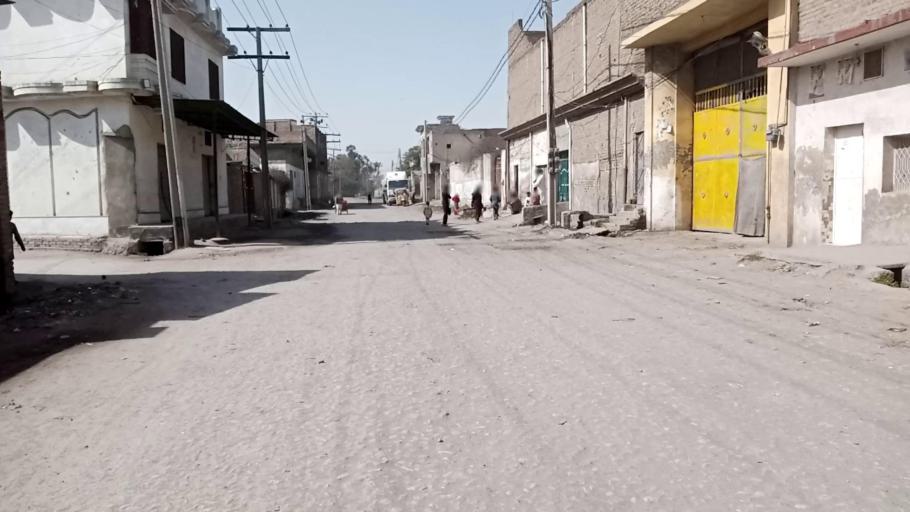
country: PK
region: Khyber Pakhtunkhwa
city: Peshawar
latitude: 34.0181
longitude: 71.6456
